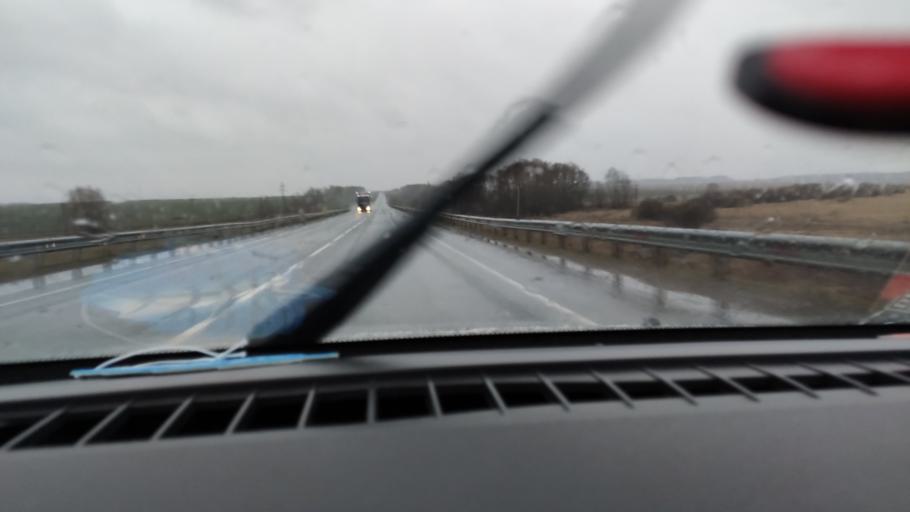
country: RU
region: Tatarstan
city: Mendeleyevsk
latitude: 55.9365
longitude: 52.2871
